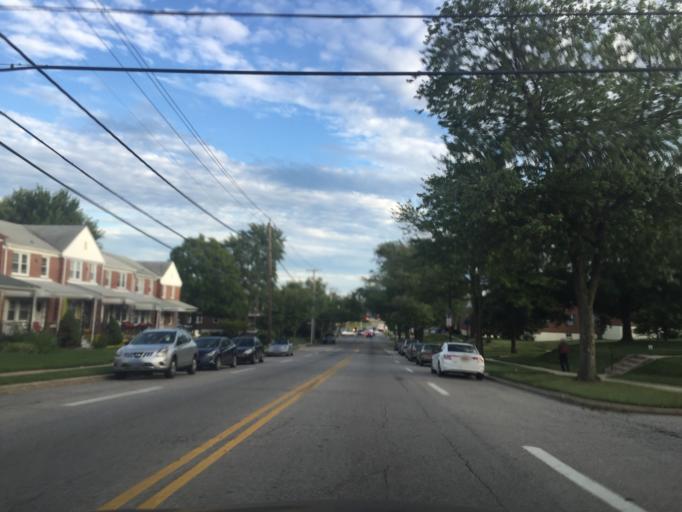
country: US
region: Maryland
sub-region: Baltimore County
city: Towson
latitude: 39.3624
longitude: -76.5940
